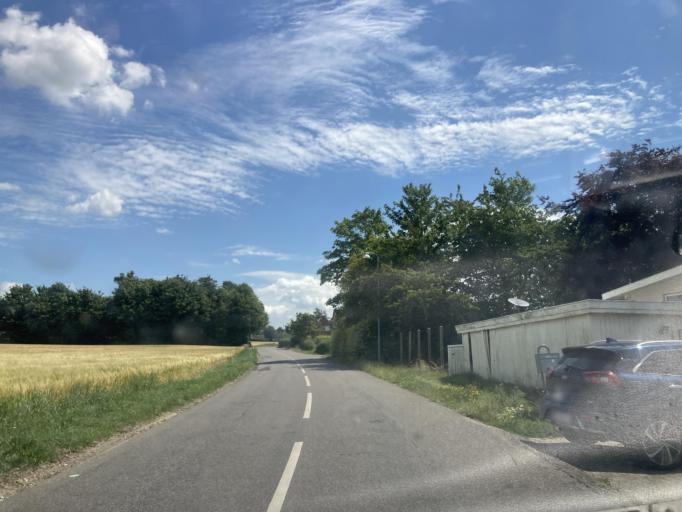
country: DK
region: Zealand
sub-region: Faxe Kommune
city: Haslev
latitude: 55.3778
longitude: 11.9579
